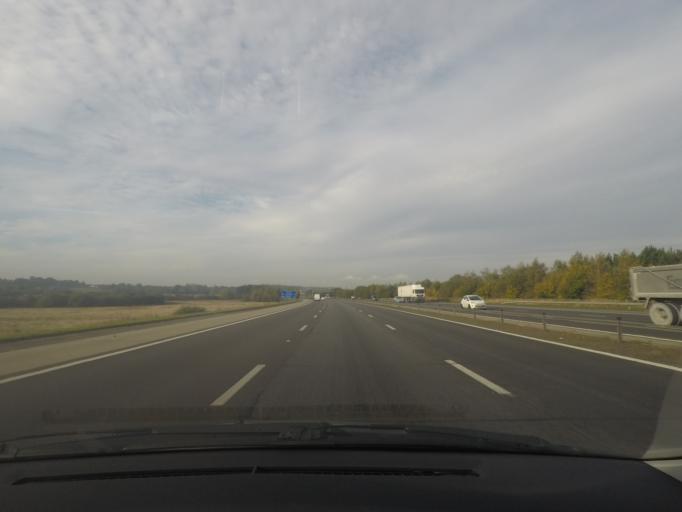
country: GB
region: England
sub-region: City and Borough of Leeds
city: Garforth
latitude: 53.8060
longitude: -1.3770
